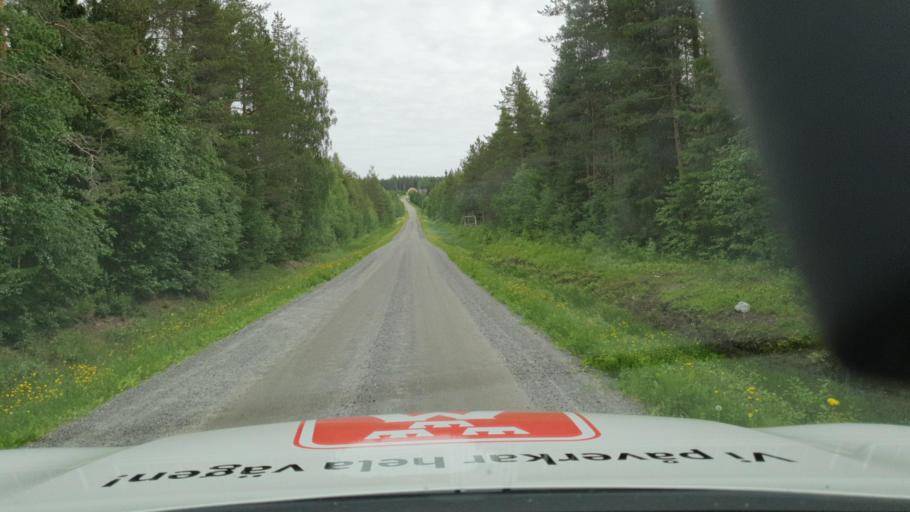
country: SE
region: Vaesterbotten
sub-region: Skelleftea Kommun
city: Langsele
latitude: 64.4774
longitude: 20.2290
